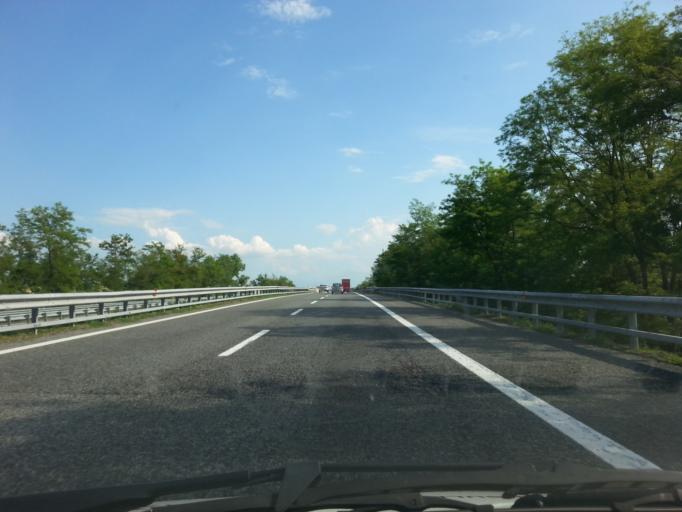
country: IT
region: Piedmont
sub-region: Provincia di Cuneo
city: Marene
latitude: 44.6969
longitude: 7.7651
